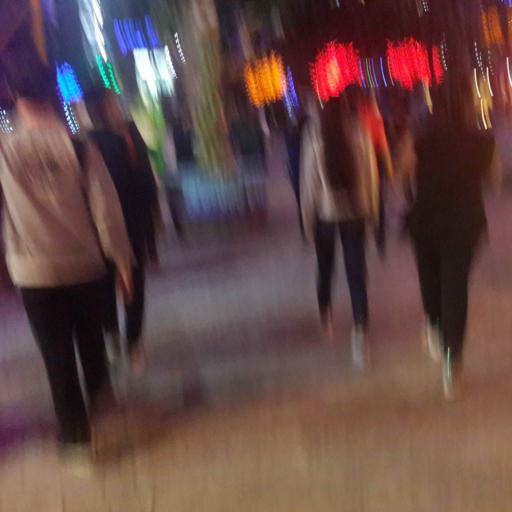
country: MY
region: Selangor
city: Klang
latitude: 3.0647
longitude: 101.4829
